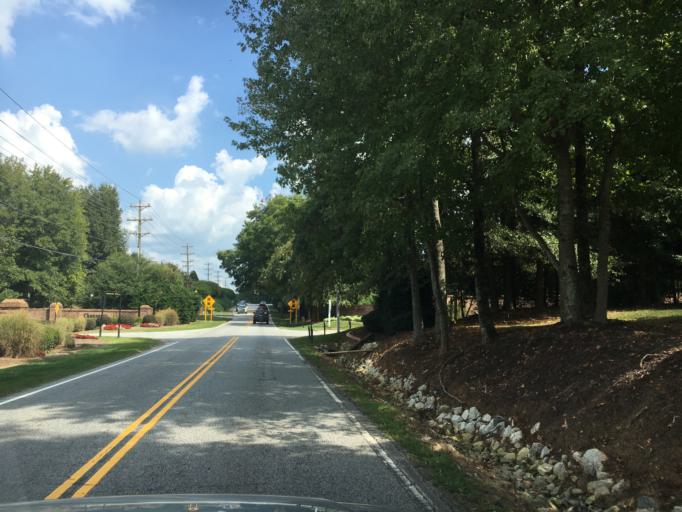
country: US
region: South Carolina
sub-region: Greenville County
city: Five Forks
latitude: 34.8296
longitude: -82.2581
